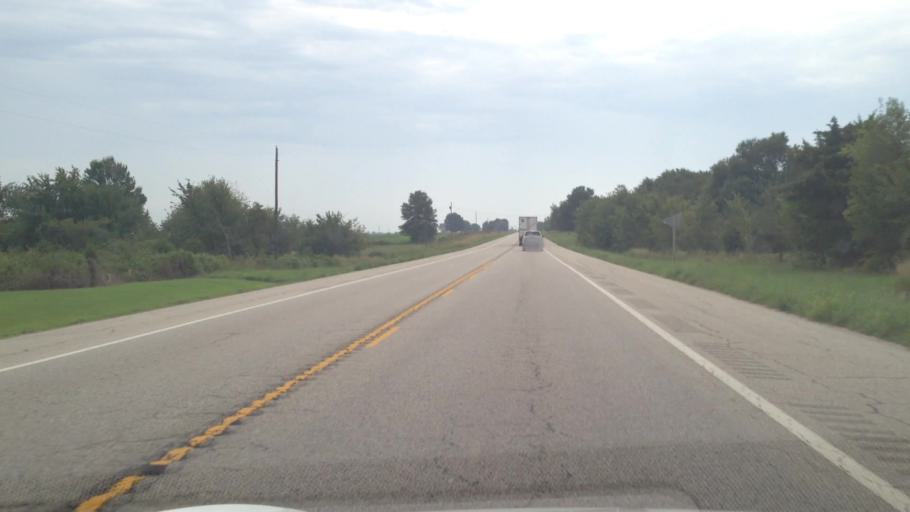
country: US
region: Kansas
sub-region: Crawford County
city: Pittsburg
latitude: 37.2876
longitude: -94.7055
